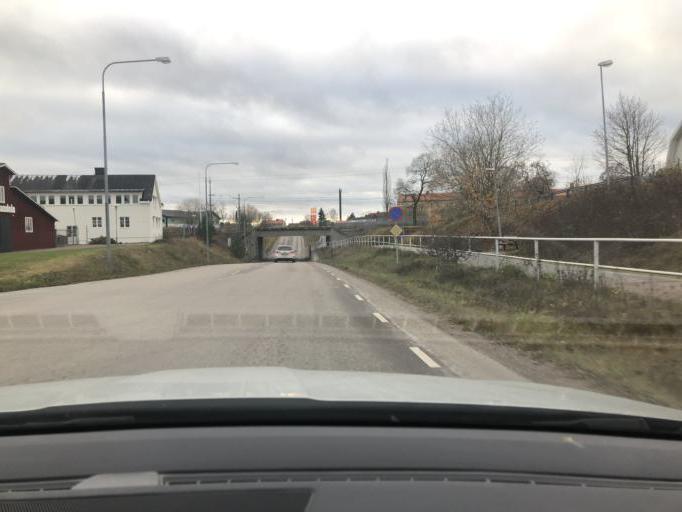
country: SE
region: Uppsala
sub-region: Tierps Kommun
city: Tierp
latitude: 60.3433
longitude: 17.5215
